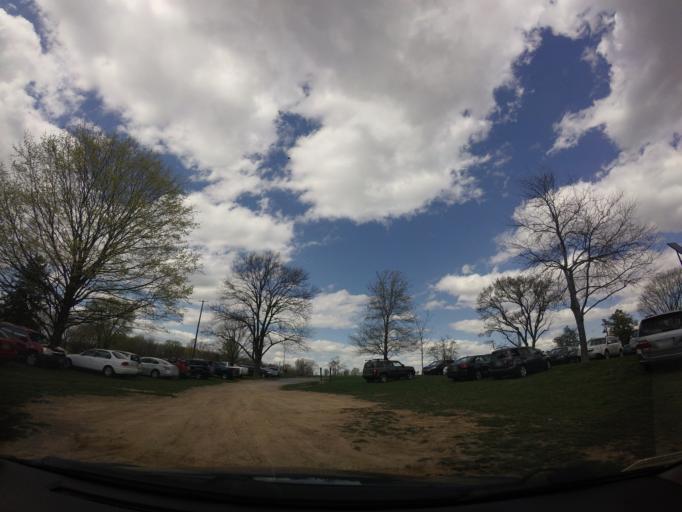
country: US
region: Maryland
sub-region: Washington County
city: Keedysville
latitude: 39.4739
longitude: -77.7455
